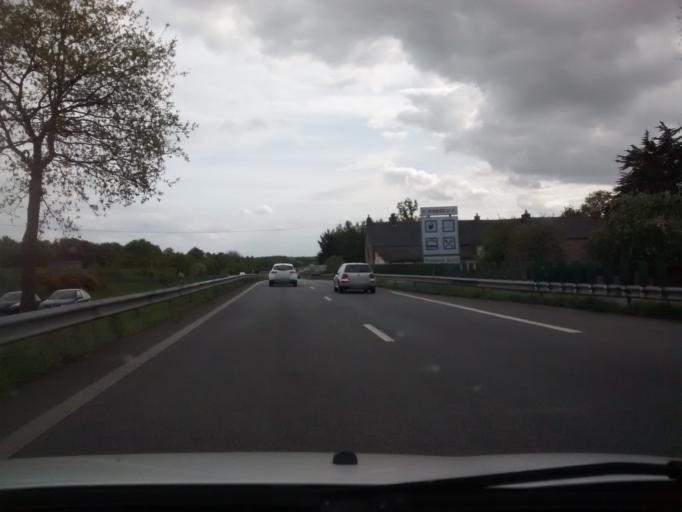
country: FR
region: Brittany
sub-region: Departement d'Ille-et-Vilaine
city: Saint-Pierre-de-Plesguen
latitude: 48.4702
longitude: -1.9125
